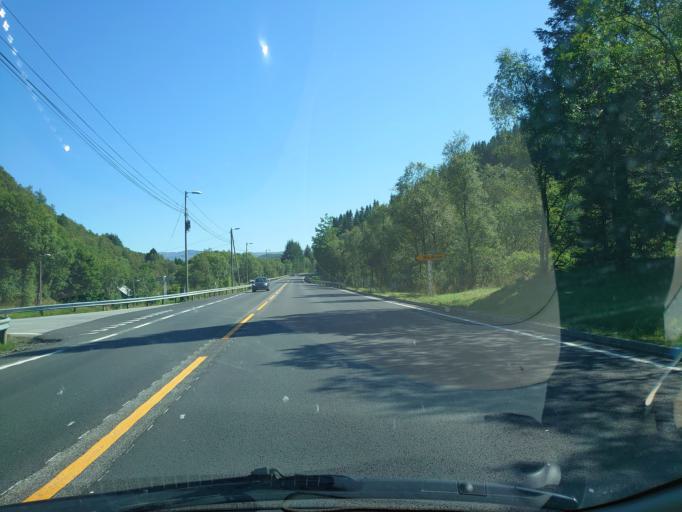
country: NO
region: Hordaland
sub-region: Bergen
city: Hylkje
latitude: 60.4687
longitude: 5.3716
